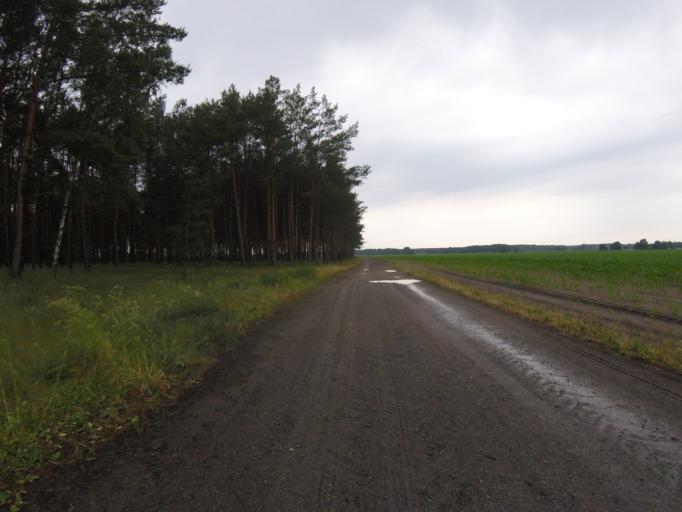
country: DE
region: Brandenburg
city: Schlepzig
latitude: 52.0332
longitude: 13.9693
